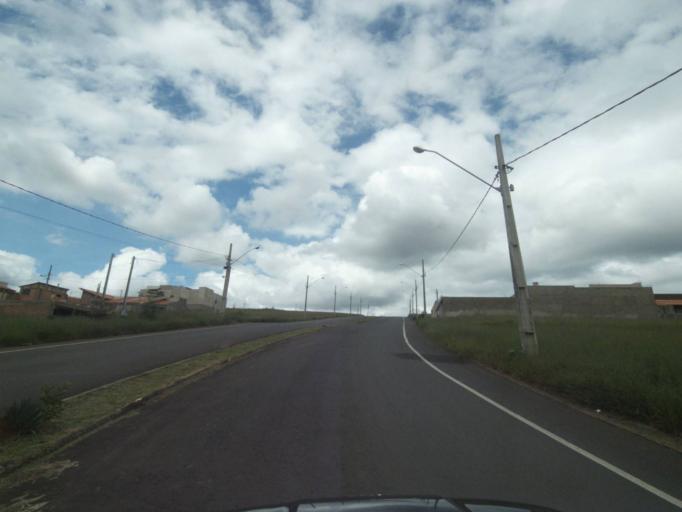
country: BR
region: Parana
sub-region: Telemaco Borba
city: Telemaco Borba
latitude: -24.3135
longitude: -50.6399
